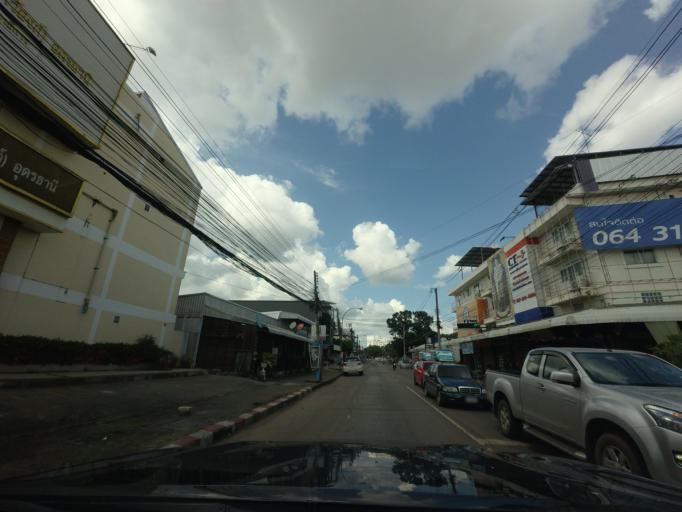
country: TH
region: Changwat Udon Thani
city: Udon Thani
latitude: 17.4111
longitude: 102.7759
